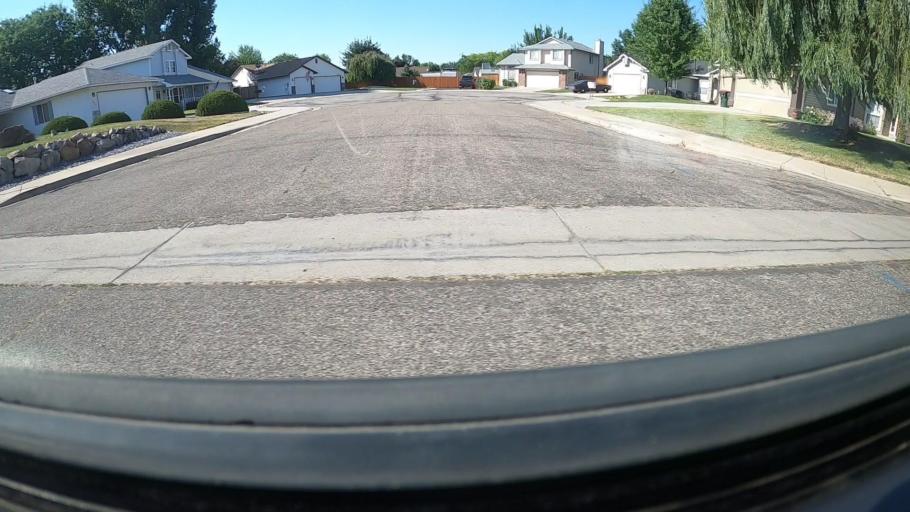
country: US
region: Idaho
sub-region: Ada County
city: Meridian
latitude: 43.6234
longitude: -116.3711
